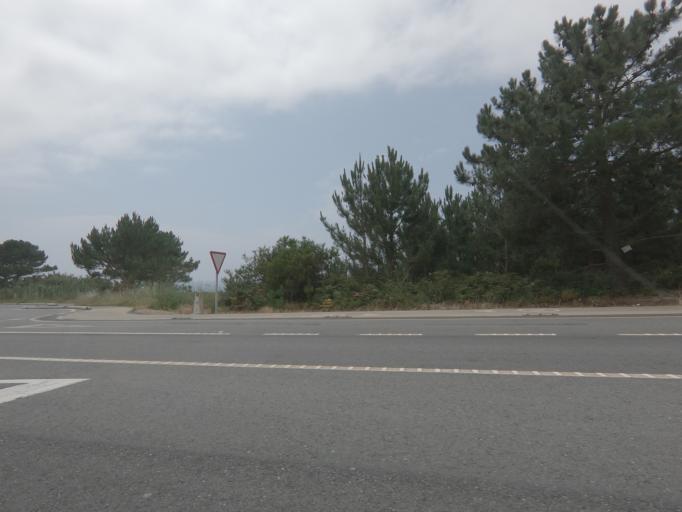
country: ES
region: Galicia
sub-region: Provincia de Pontevedra
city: Oia
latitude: 41.9723
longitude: -8.8843
